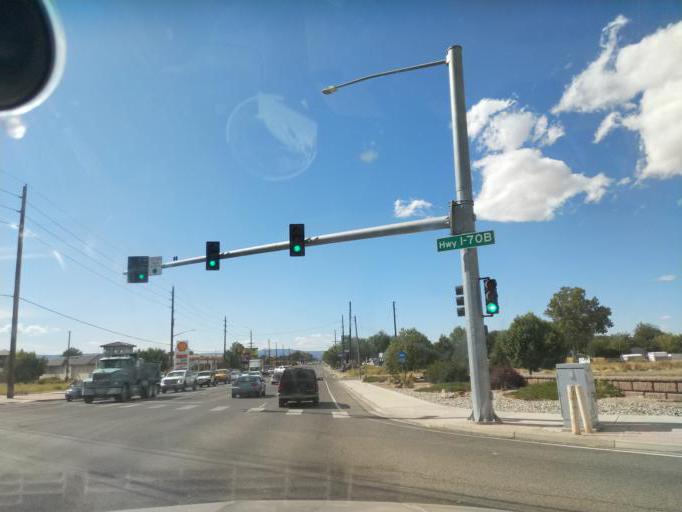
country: US
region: Colorado
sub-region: Mesa County
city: Clifton
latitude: 39.0919
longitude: -108.4533
